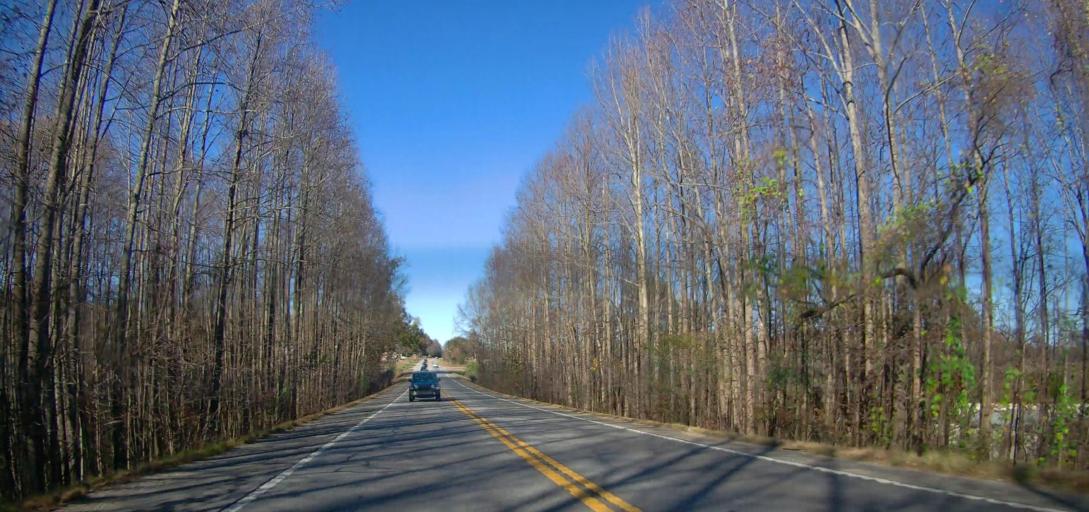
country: US
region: Georgia
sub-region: White County
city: Cleveland
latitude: 34.5161
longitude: -83.7550
